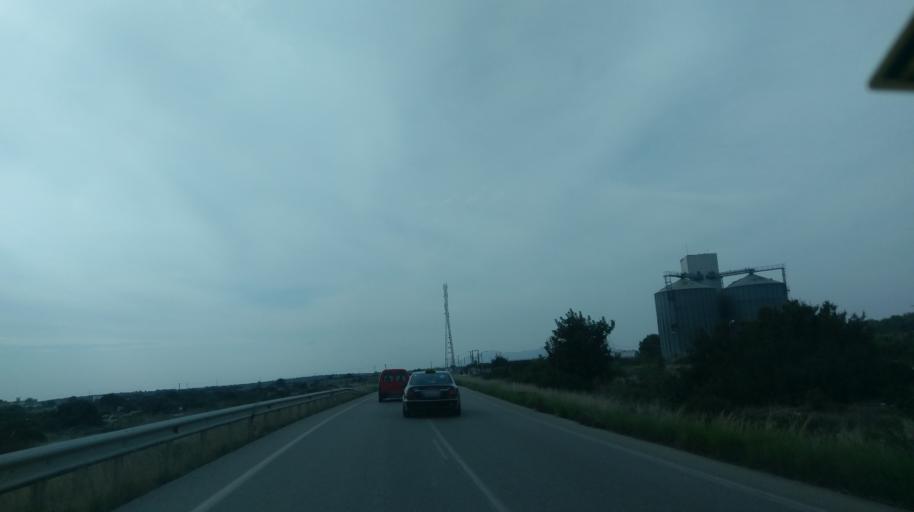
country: CY
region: Ammochostos
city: Leonarisso
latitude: 35.4337
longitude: 34.1323
